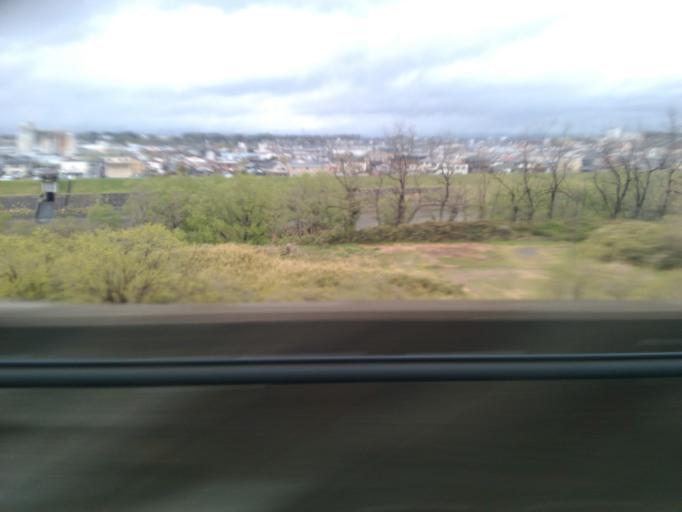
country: JP
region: Fukushima
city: Koriyama
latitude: 37.3532
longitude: 140.3727
